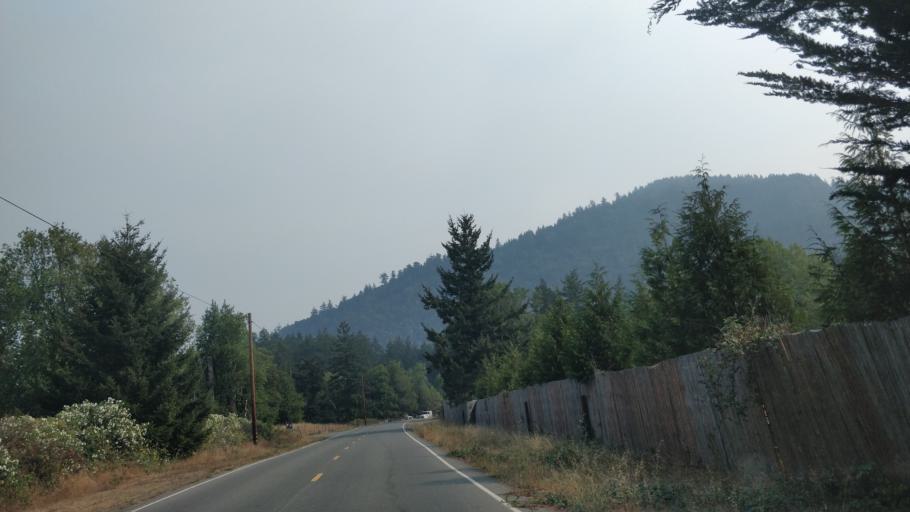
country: US
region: California
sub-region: Humboldt County
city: Rio Dell
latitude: 40.3182
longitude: -124.2848
